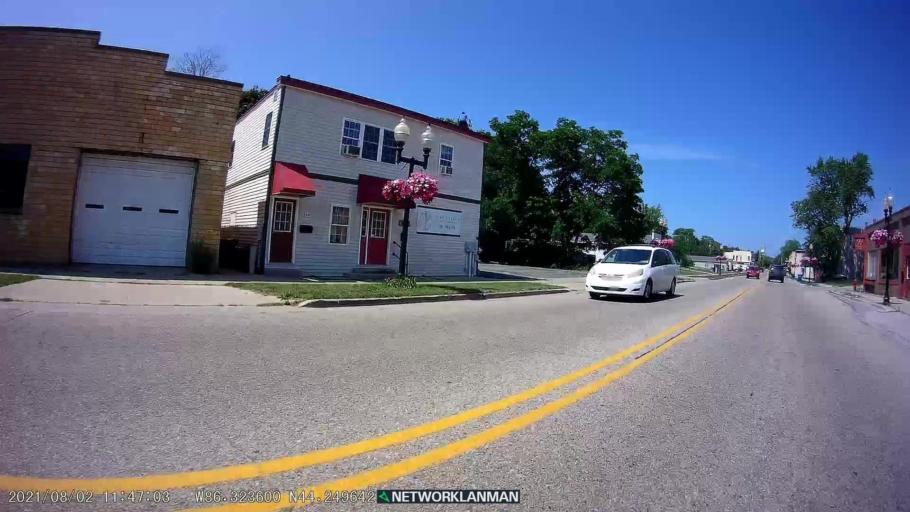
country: US
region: Michigan
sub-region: Manistee County
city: Manistee
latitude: 44.2498
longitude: -86.3236
